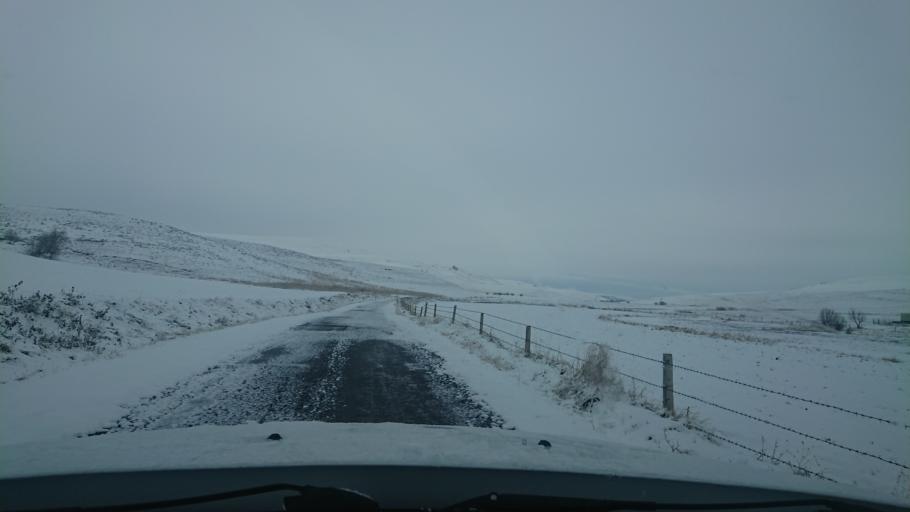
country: TR
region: Aksaray
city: Acipinar
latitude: 38.6809
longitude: 33.8643
